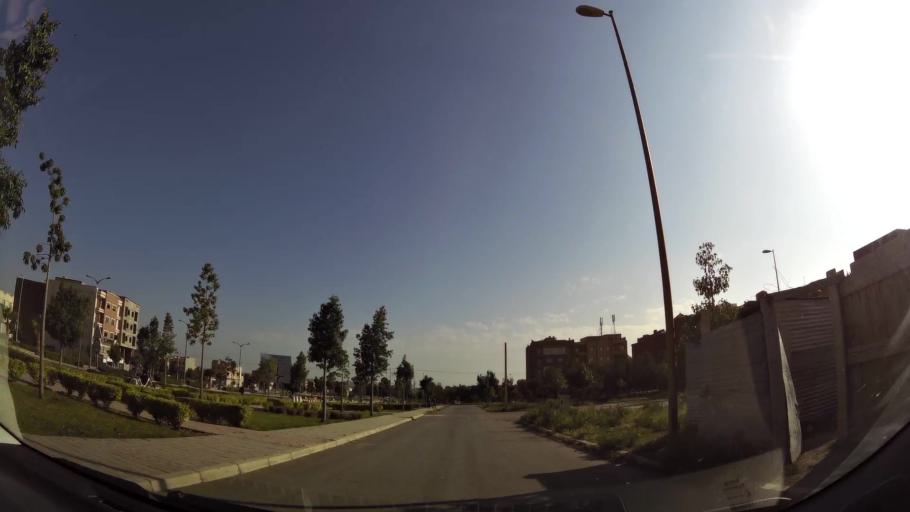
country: MA
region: Oriental
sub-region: Oujda-Angad
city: Oujda
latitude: 34.6812
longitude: -1.9464
